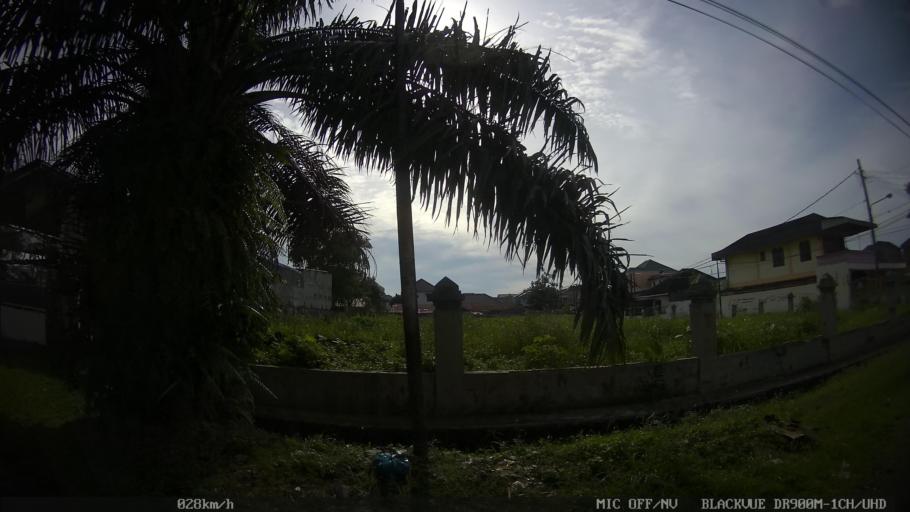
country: ID
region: North Sumatra
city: Sunggal
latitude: 3.6097
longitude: 98.6290
